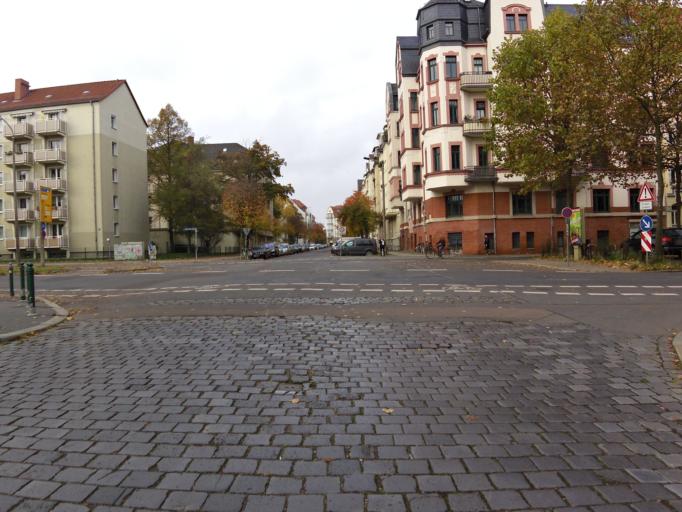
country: DE
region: Saxony
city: Leipzig
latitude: 51.3207
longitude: 12.3657
